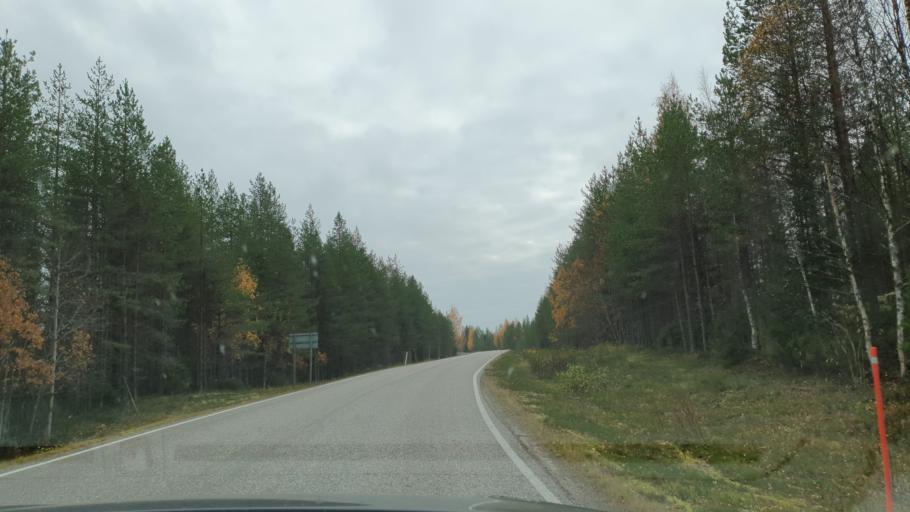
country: FI
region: Kainuu
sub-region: Kajaani
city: Paltamo
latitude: 64.6485
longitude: 27.9650
